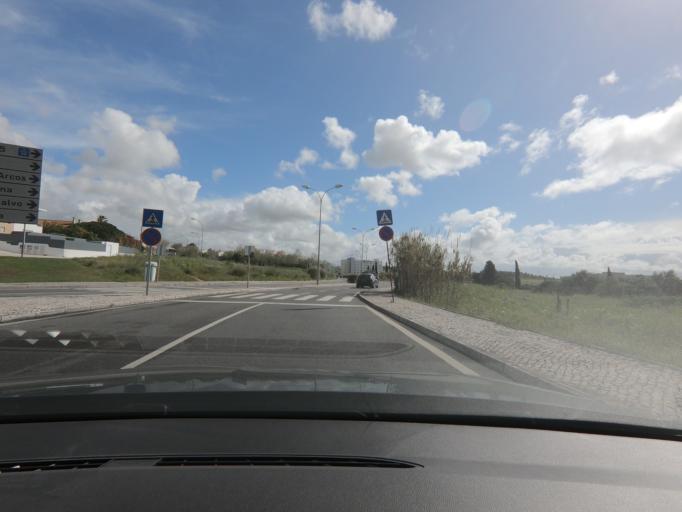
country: PT
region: Lisbon
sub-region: Oeiras
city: Porto Salvo
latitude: 38.7139
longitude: -9.3039
